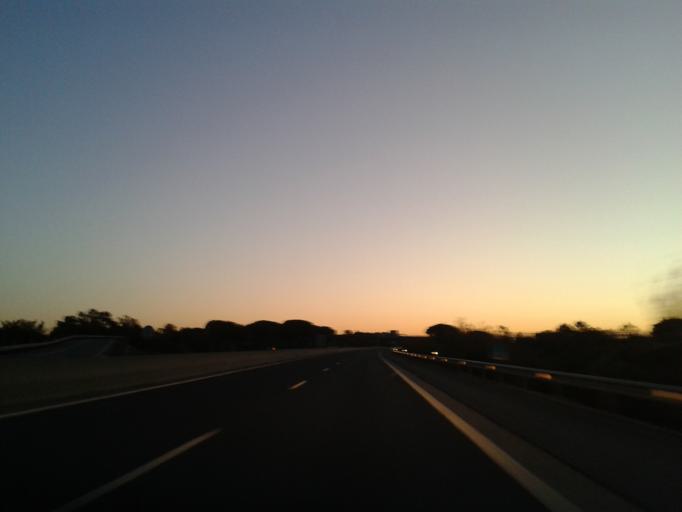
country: PT
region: Faro
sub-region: Albufeira
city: Guia
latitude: 37.1385
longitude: -8.3377
